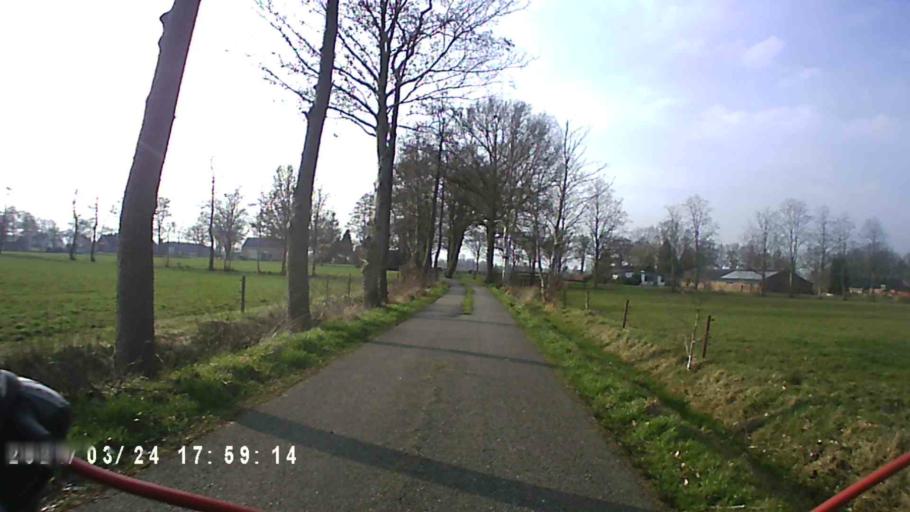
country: NL
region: Groningen
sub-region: Gemeente Leek
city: Leek
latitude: 53.1312
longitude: 6.3588
